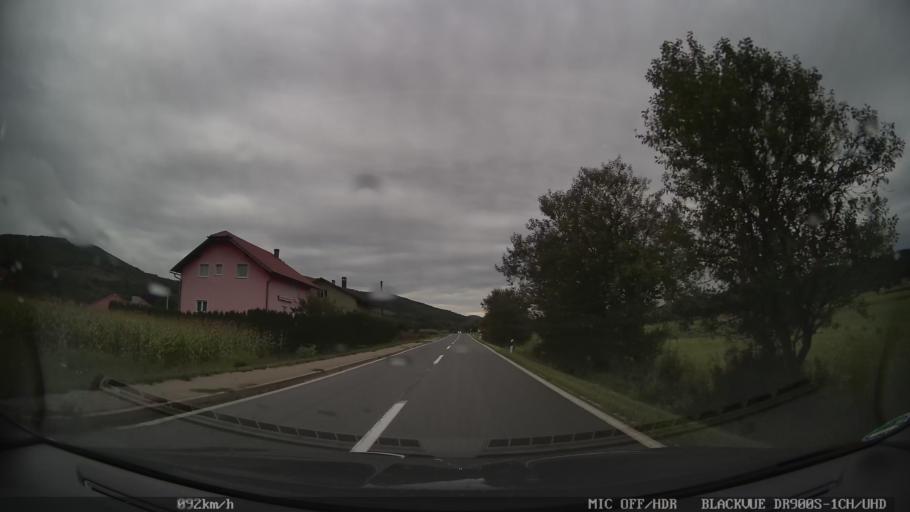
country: HR
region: Licko-Senjska
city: Otocac
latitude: 44.9107
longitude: 15.1648
